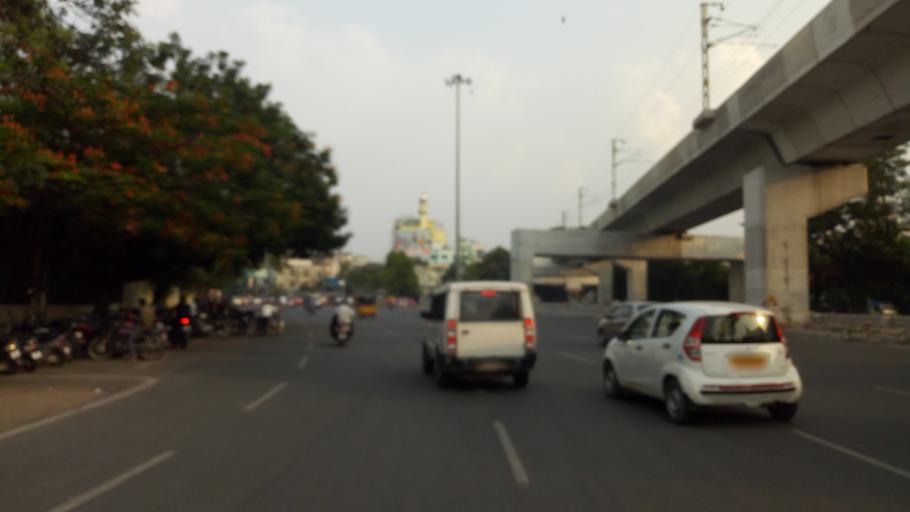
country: IN
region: Telangana
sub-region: Hyderabad
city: Hyderabad
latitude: 17.4001
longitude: 78.4707
